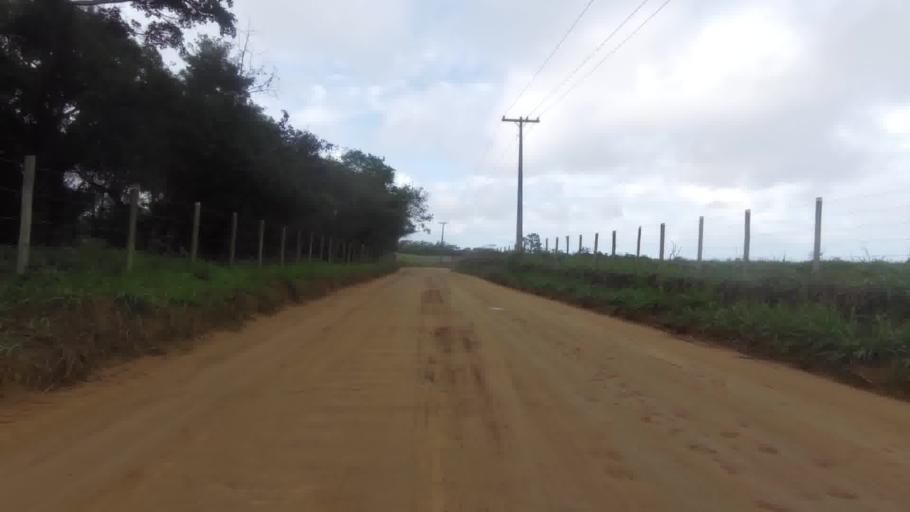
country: BR
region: Espirito Santo
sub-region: Piuma
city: Piuma
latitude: -20.7769
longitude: -40.6299
